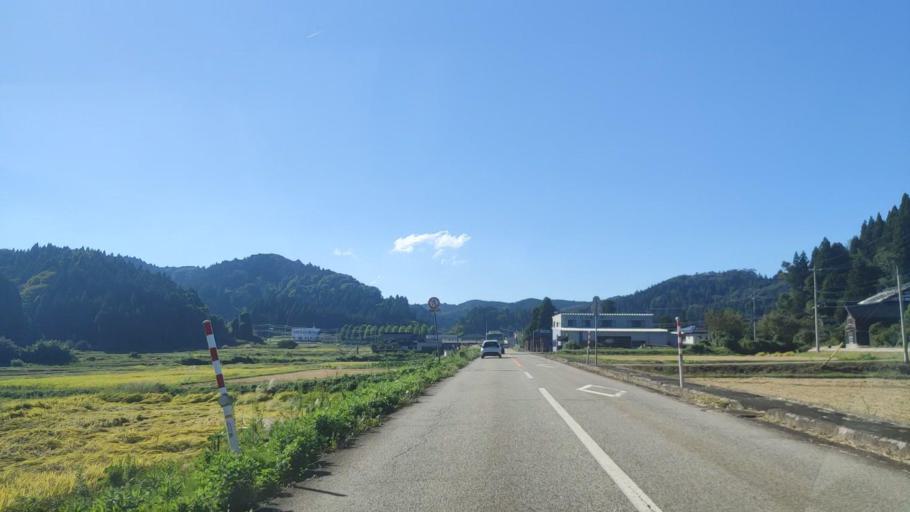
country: JP
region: Ishikawa
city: Nanao
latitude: 37.2797
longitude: 137.0473
